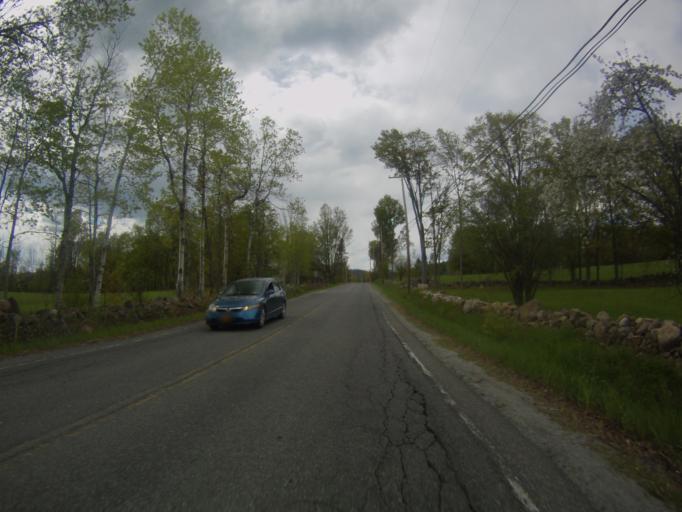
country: US
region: New York
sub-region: Essex County
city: Mineville
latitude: 44.0661
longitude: -73.5159
